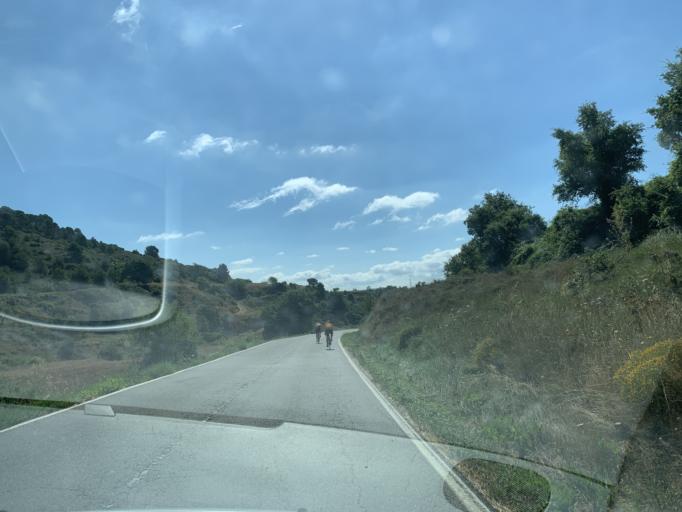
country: ES
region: Catalonia
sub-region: Provincia de Tarragona
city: Santa Coloma de Queralt
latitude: 41.5424
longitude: 1.3716
